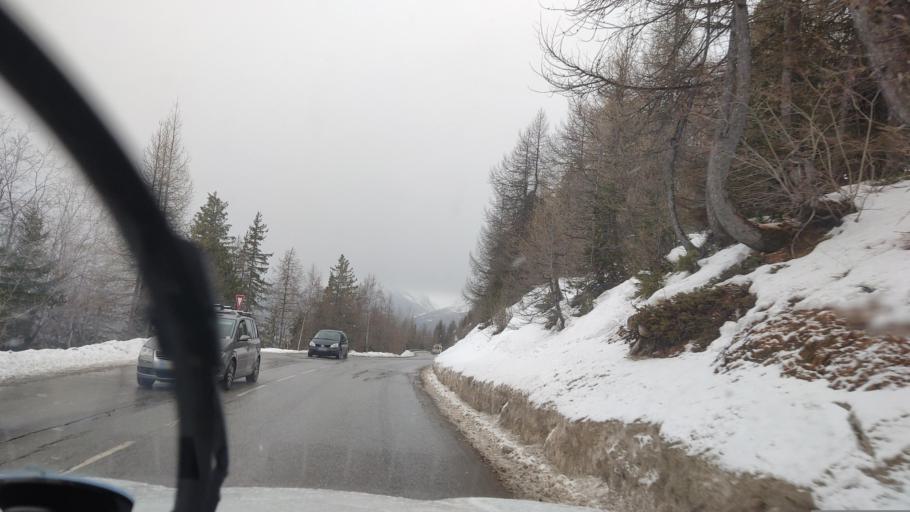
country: FR
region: Rhone-Alpes
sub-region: Departement de la Savoie
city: Belle-Plagne
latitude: 45.5104
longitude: 6.6798
